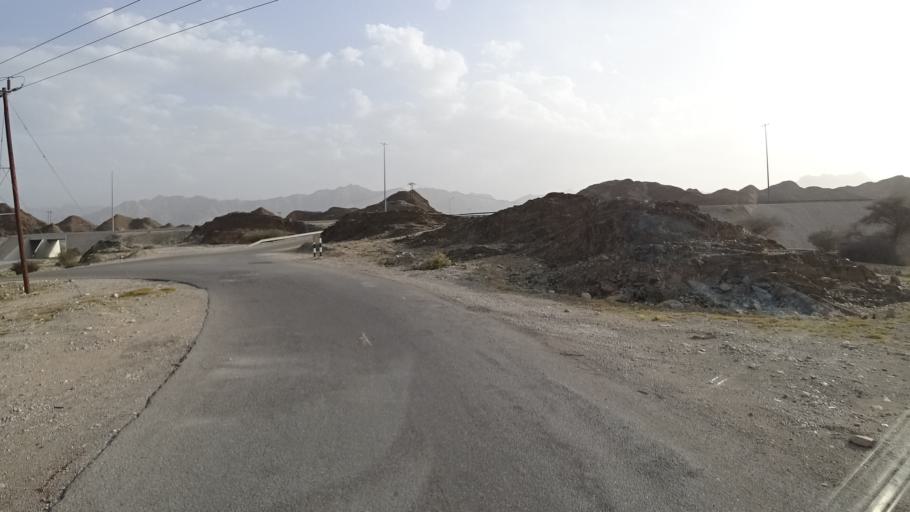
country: OM
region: Muhafazat Masqat
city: Bawshar
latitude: 23.3546
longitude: 58.5348
